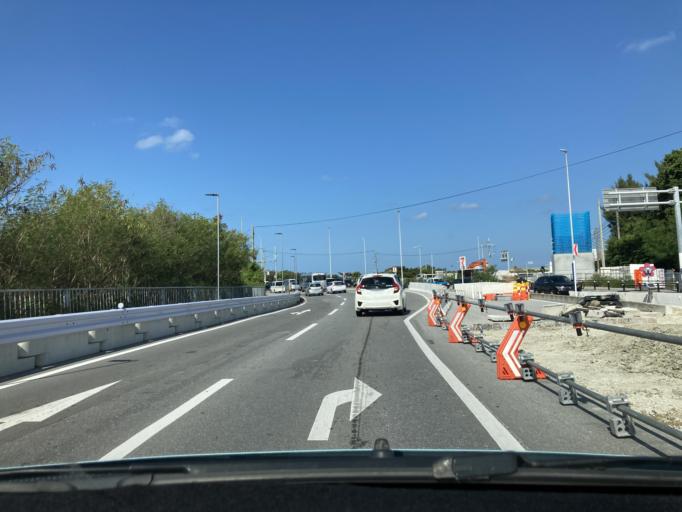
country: JP
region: Okinawa
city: Tomigusuku
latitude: 26.1748
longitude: 127.6542
